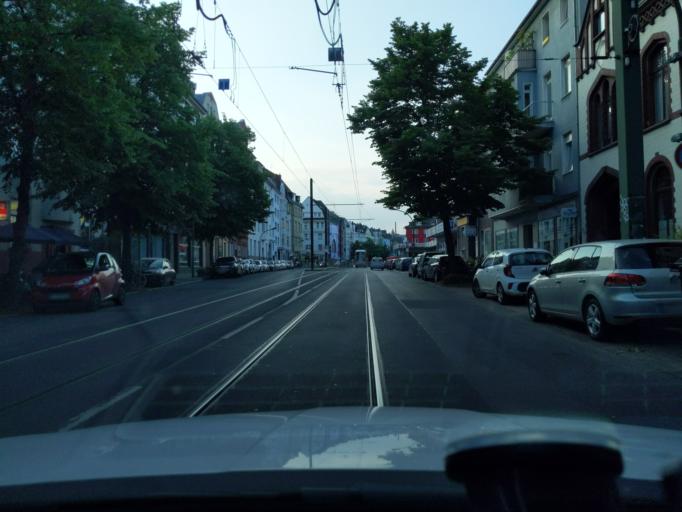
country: DE
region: North Rhine-Westphalia
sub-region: Regierungsbezirk Dusseldorf
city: Dusseldorf
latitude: 51.2012
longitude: 6.7812
